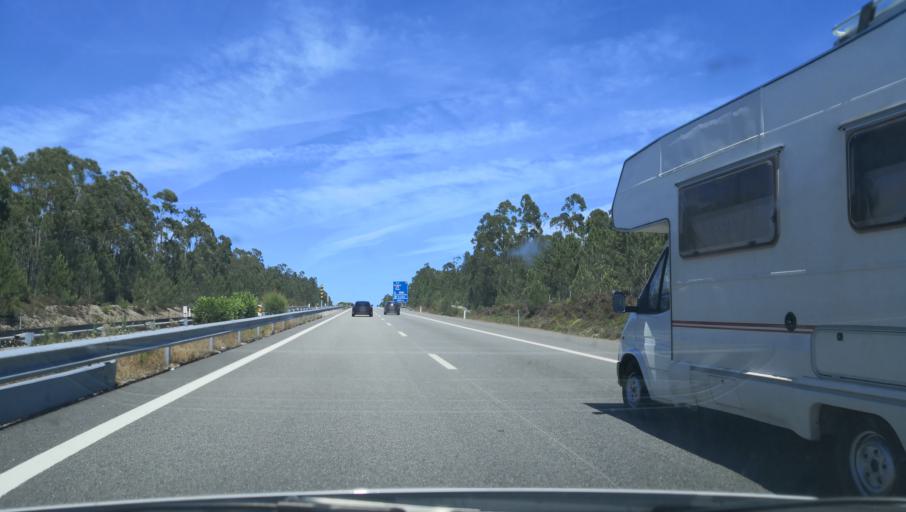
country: PT
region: Coimbra
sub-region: Montemor-O-Velho
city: Arazede
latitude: 40.2498
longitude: -8.6507
